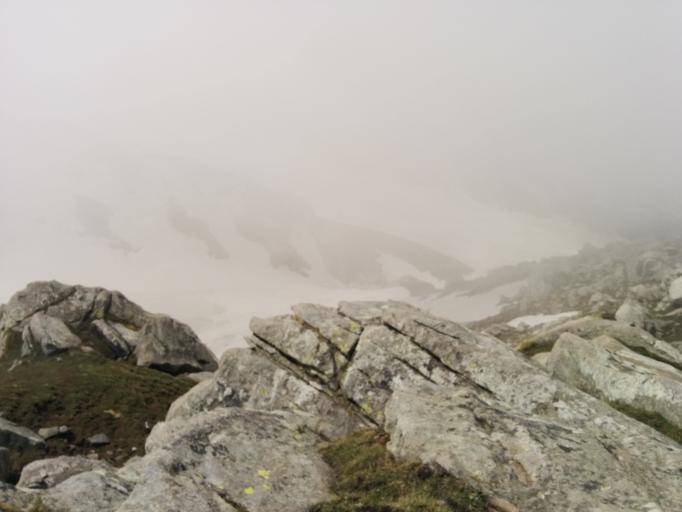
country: IN
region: Himachal Pradesh
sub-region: Kangra
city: Dharmsala
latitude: 32.2893
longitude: 76.3736
